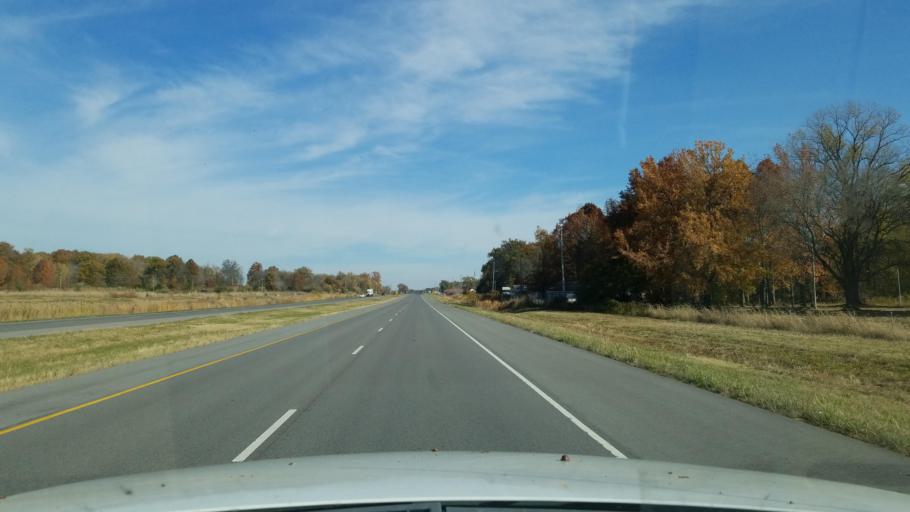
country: US
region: Illinois
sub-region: Saline County
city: Eldorado
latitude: 37.7839
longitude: -88.4892
